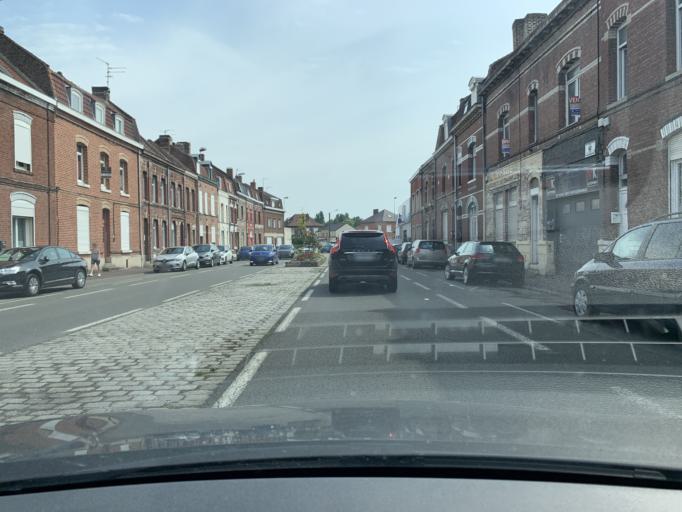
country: FR
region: Nord-Pas-de-Calais
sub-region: Departement du Nord
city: Douai
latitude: 50.3637
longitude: 3.0675
